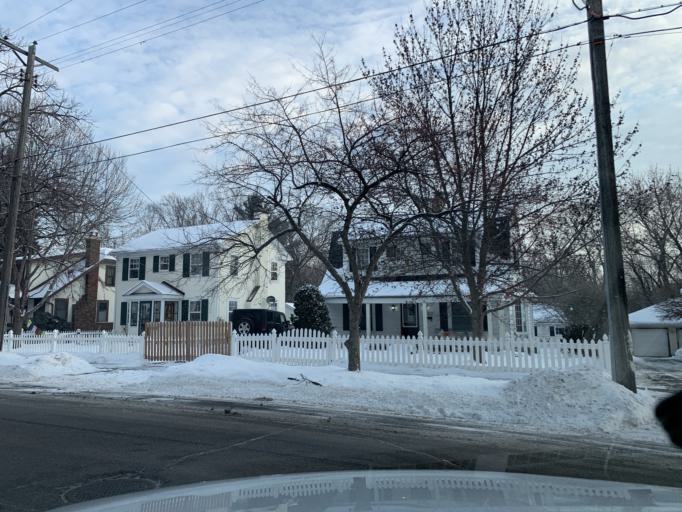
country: US
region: Minnesota
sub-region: Hennepin County
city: Saint Louis Park
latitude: 44.9260
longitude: -93.3557
